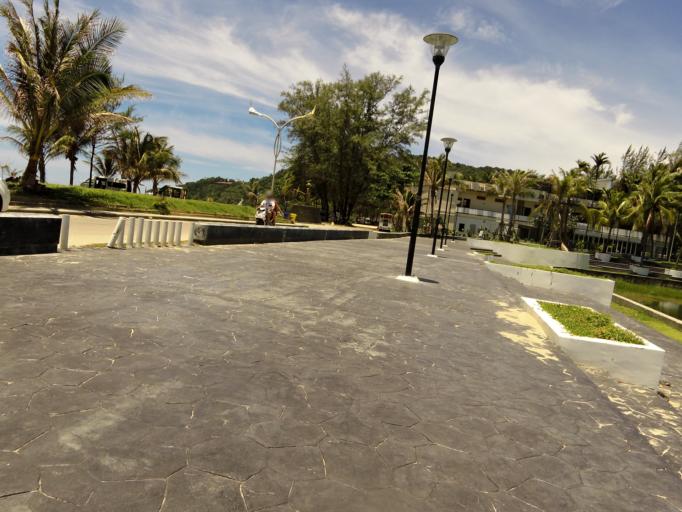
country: TH
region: Phuket
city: Ban Karon
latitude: 7.8525
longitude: 98.2923
